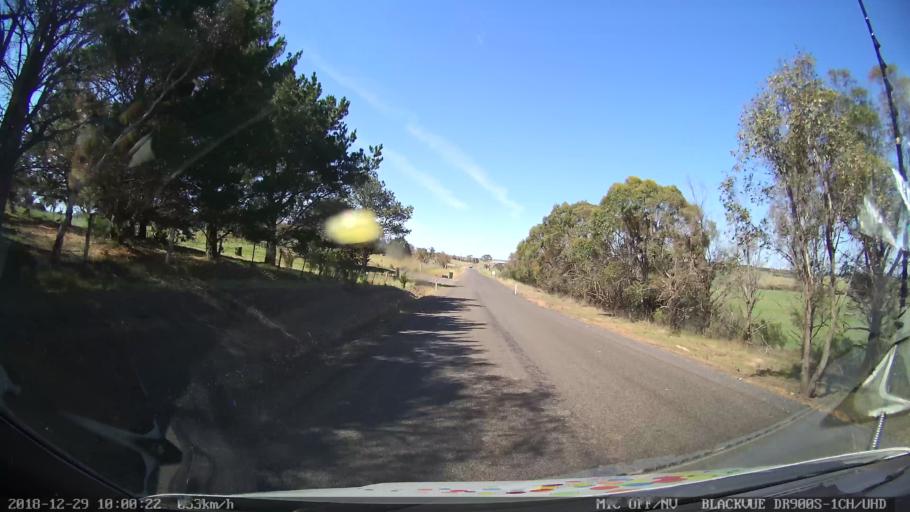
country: AU
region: New South Wales
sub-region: Goulburn Mulwaree
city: Goulburn
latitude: -34.7916
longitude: 149.4859
